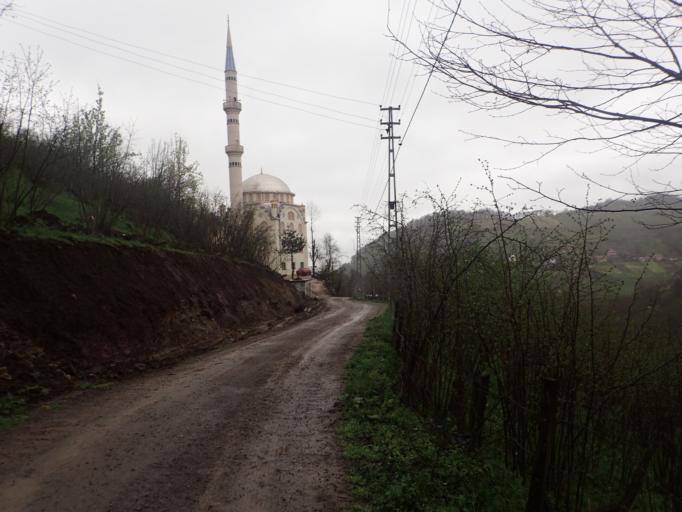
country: TR
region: Ordu
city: Korgan
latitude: 40.8030
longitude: 37.2816
